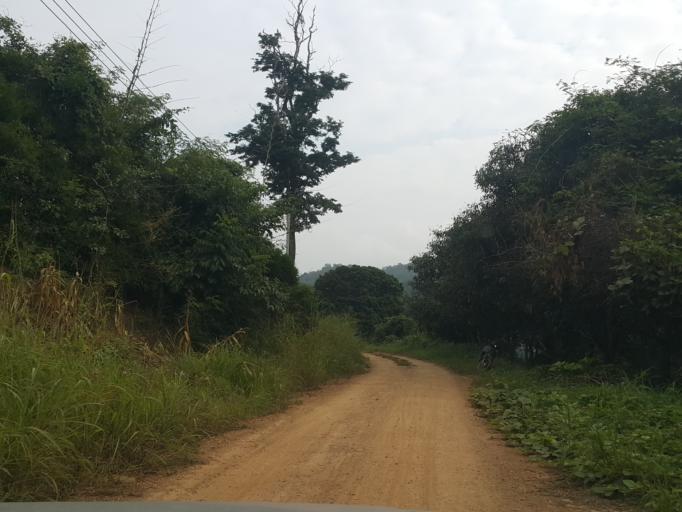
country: TH
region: Mae Hong Son
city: Wiang Nuea
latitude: 19.3877
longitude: 98.4664
